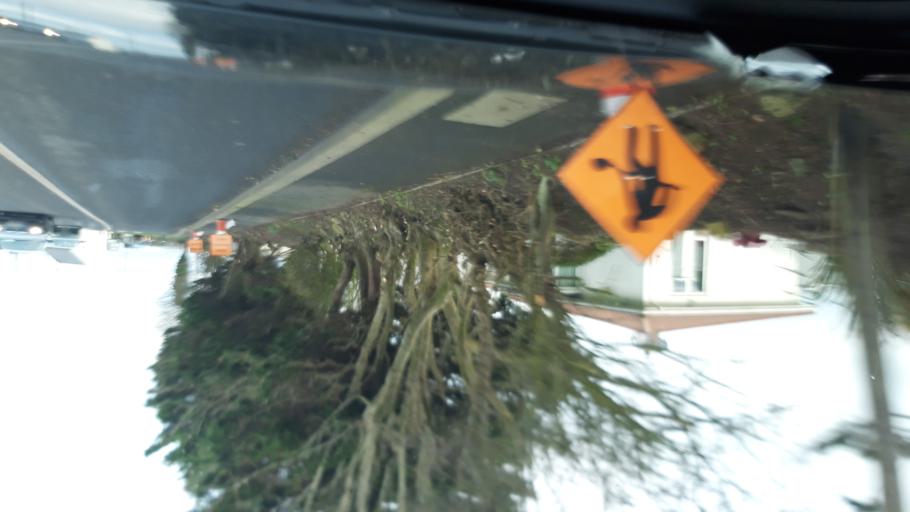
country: IE
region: Leinster
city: An Ros
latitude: 53.5460
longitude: -6.1003
